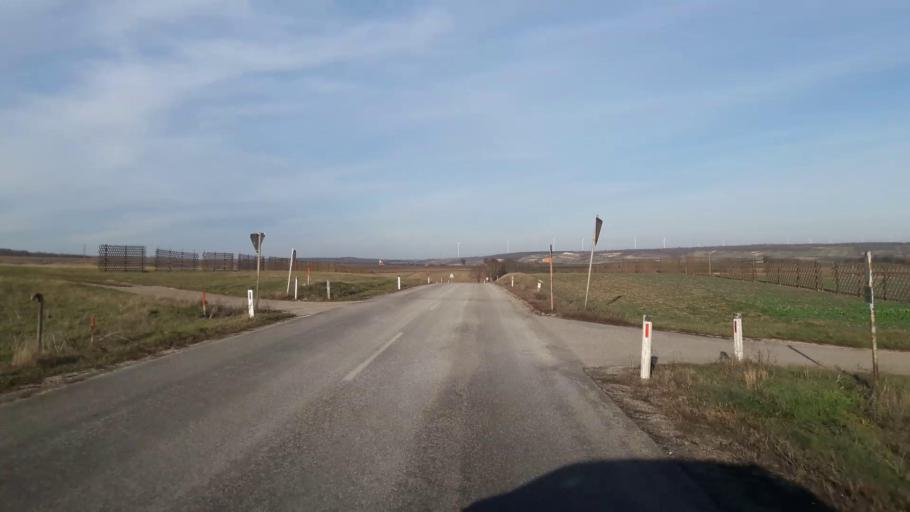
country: AT
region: Lower Austria
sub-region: Politischer Bezirk Ganserndorf
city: Auersthal
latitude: 48.3841
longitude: 16.6304
